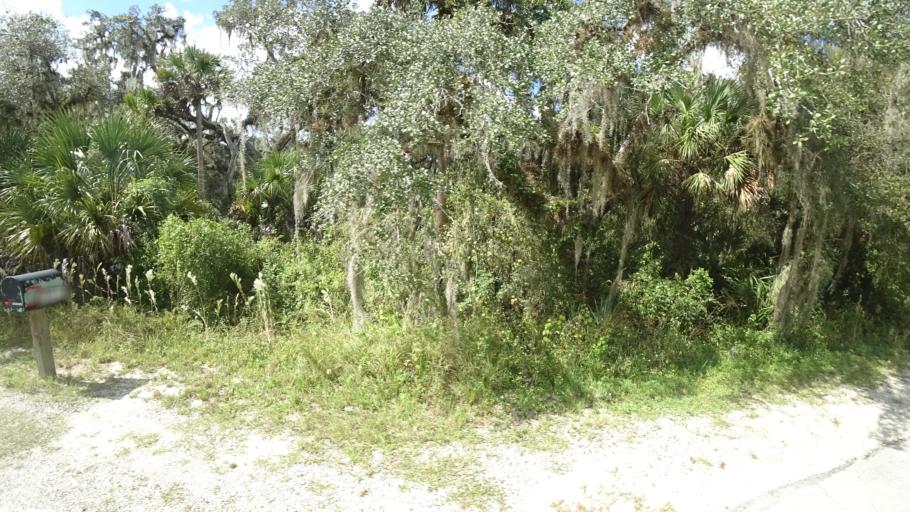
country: US
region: Florida
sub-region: Sarasota County
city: Lake Sarasota
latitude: 27.2906
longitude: -82.2531
